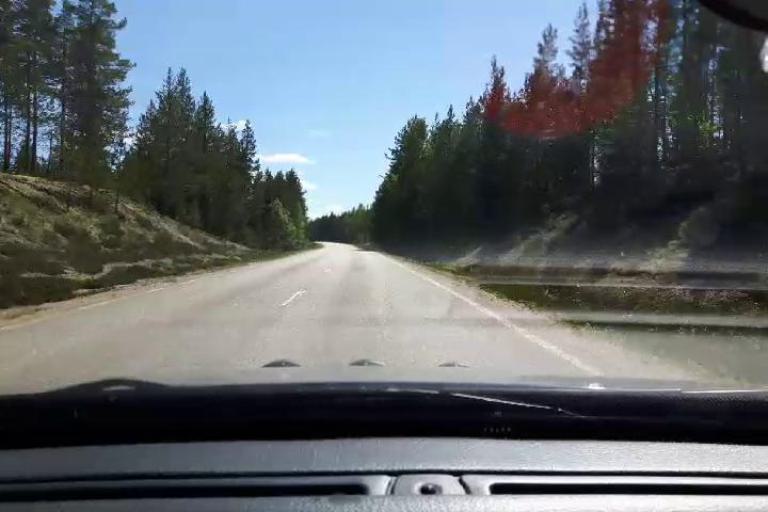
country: SE
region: Vaesternorrland
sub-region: Ange Kommun
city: Ange
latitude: 62.0715
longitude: 15.1030
